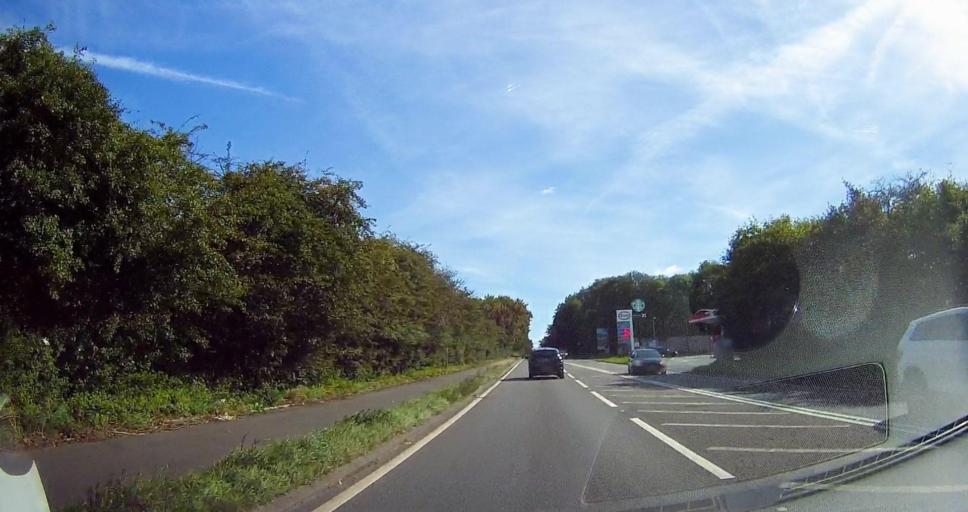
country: GB
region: England
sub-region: Staffordshire
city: Norton Canes
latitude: 52.6595
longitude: -1.9693
